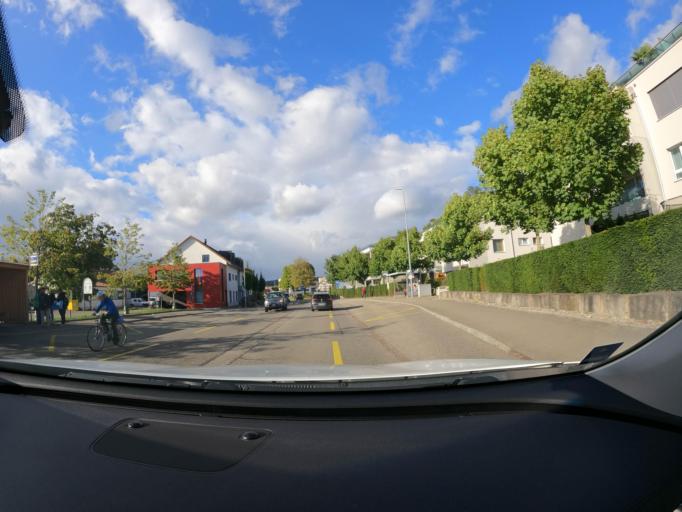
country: CH
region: Aargau
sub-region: Bezirk Brugg
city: Hausen
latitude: 47.4646
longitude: 8.2115
